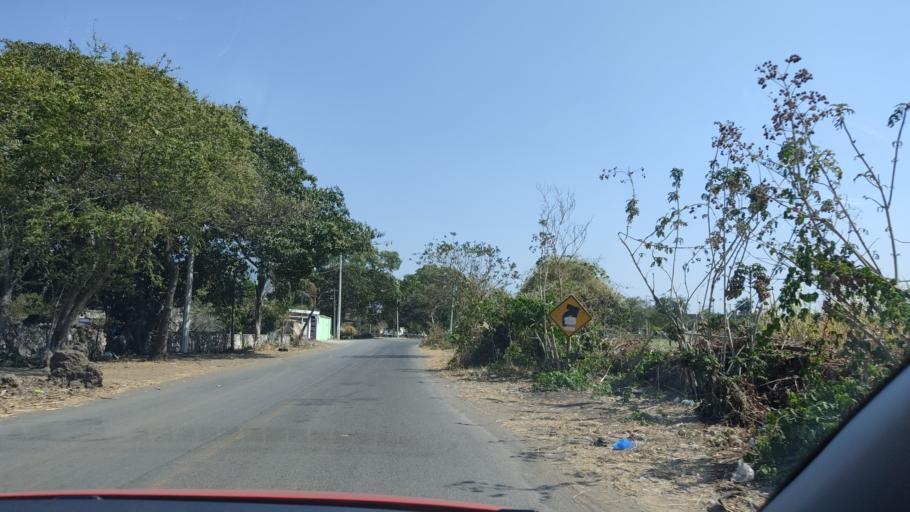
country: MX
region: Nayarit
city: Puga
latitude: 21.5309
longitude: -104.8073
